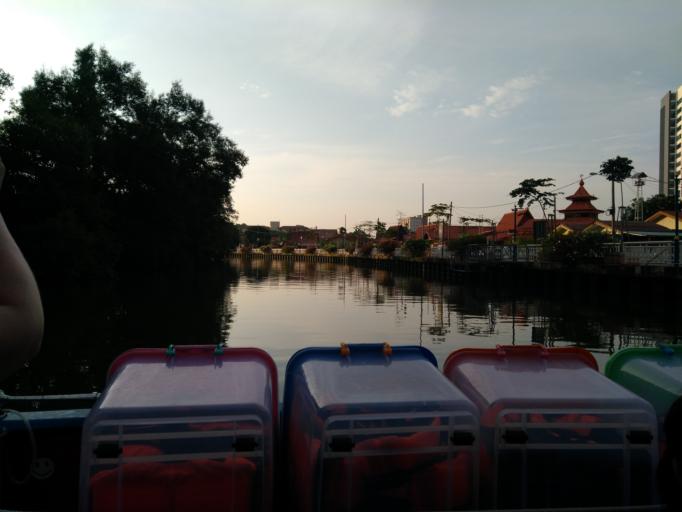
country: MY
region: Melaka
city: Malacca
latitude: 2.2025
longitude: 102.2510
